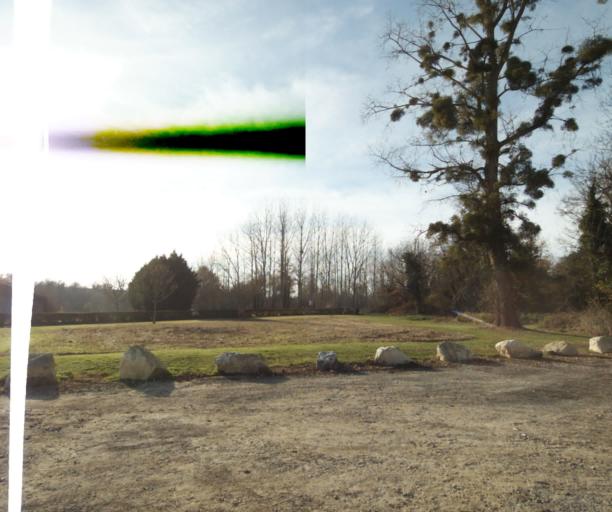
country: FR
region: Poitou-Charentes
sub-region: Departement de la Charente-Maritime
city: Burie
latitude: 45.8028
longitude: -0.4479
